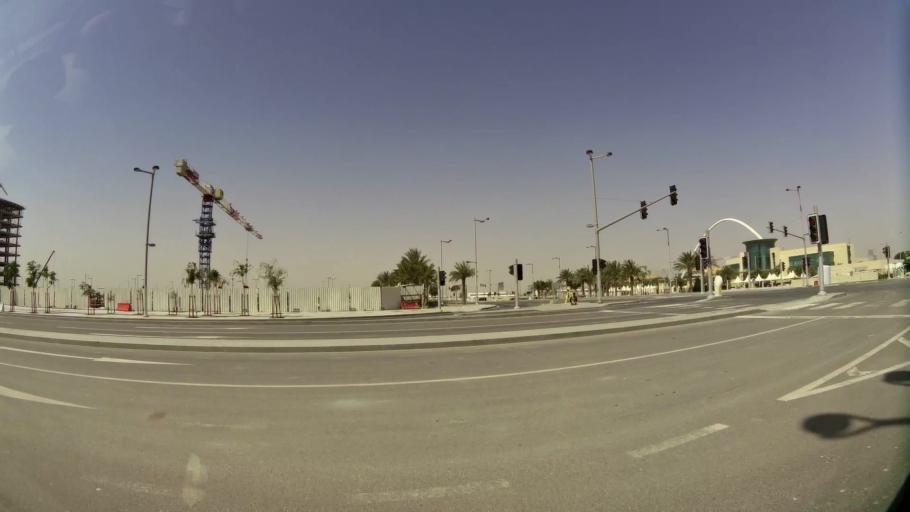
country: QA
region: Baladiyat Umm Salal
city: Umm Salal Muhammad
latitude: 25.3984
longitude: 51.5189
